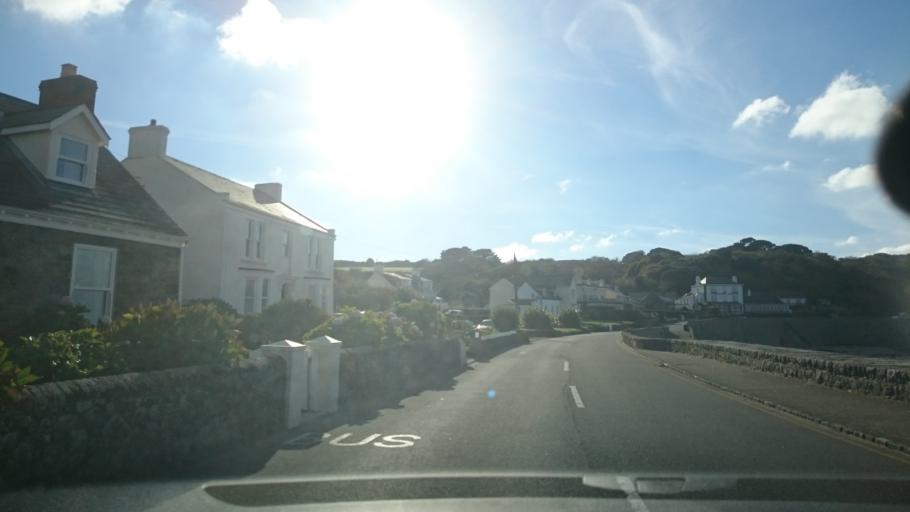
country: GG
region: St Peter Port
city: Saint Peter Port
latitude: 49.4346
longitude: -2.6569
